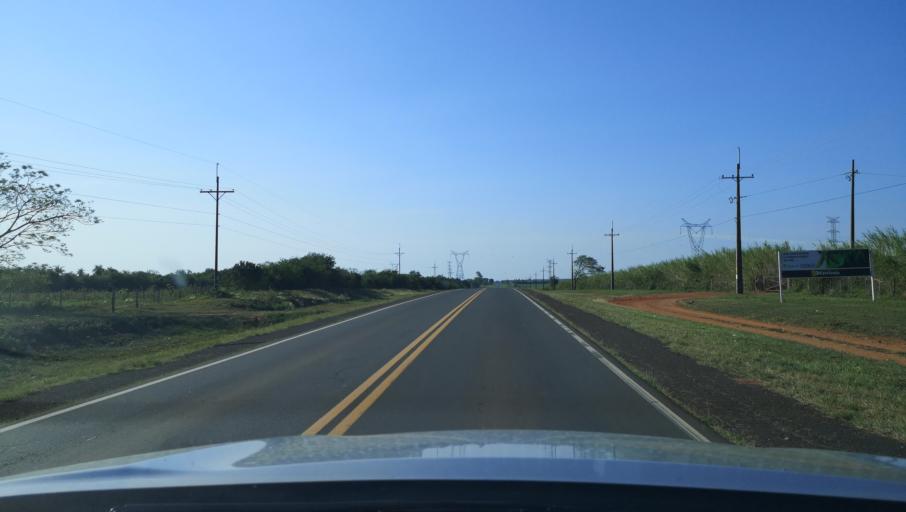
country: PY
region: Misiones
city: Santa Maria
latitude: -26.7963
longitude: -57.0230
